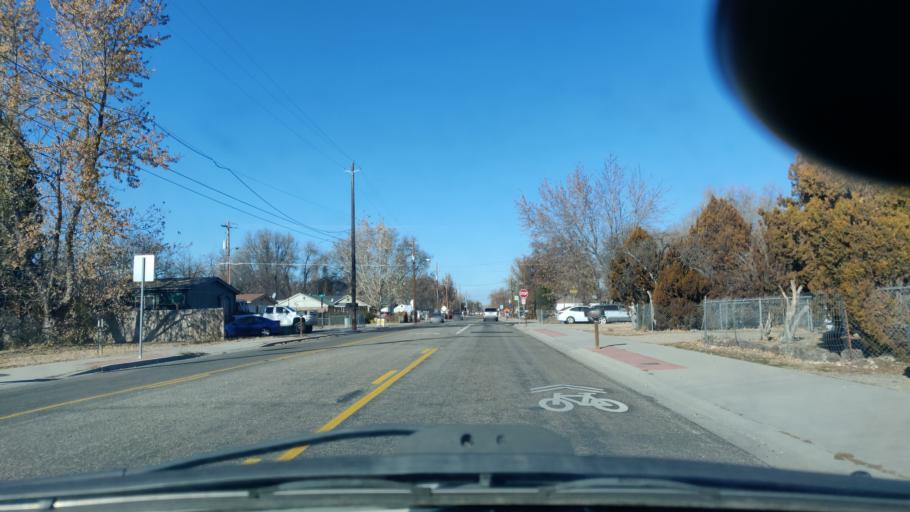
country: US
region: Idaho
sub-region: Ada County
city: Garden City
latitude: 43.6365
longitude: -116.2499
